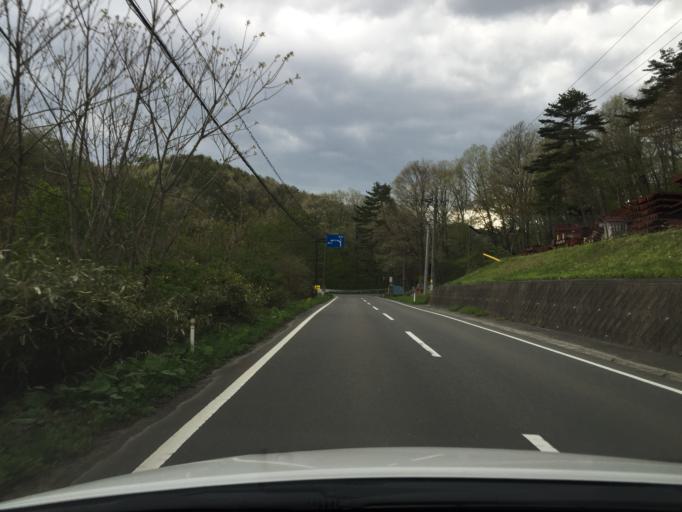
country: JP
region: Fukushima
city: Yanagawamachi-saiwaicho
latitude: 37.7235
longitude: 140.7303
